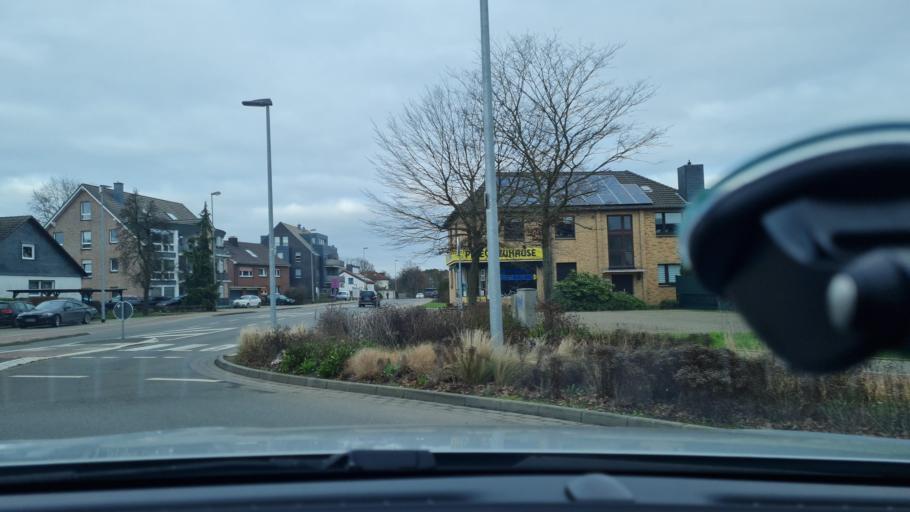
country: DE
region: North Rhine-Westphalia
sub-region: Regierungsbezirk Dusseldorf
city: Voerde
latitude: 51.5954
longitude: 6.6845
